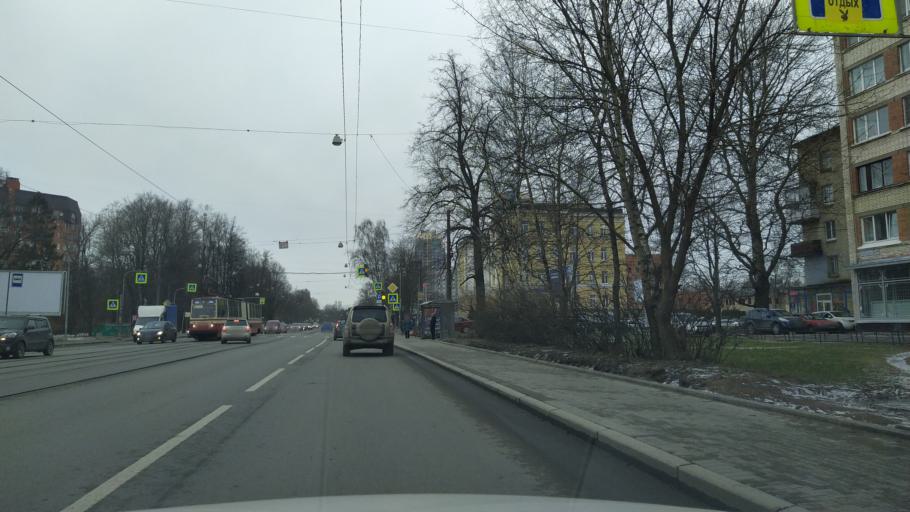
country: RU
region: Leningrad
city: Udel'naya
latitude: 60.0202
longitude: 30.3211
